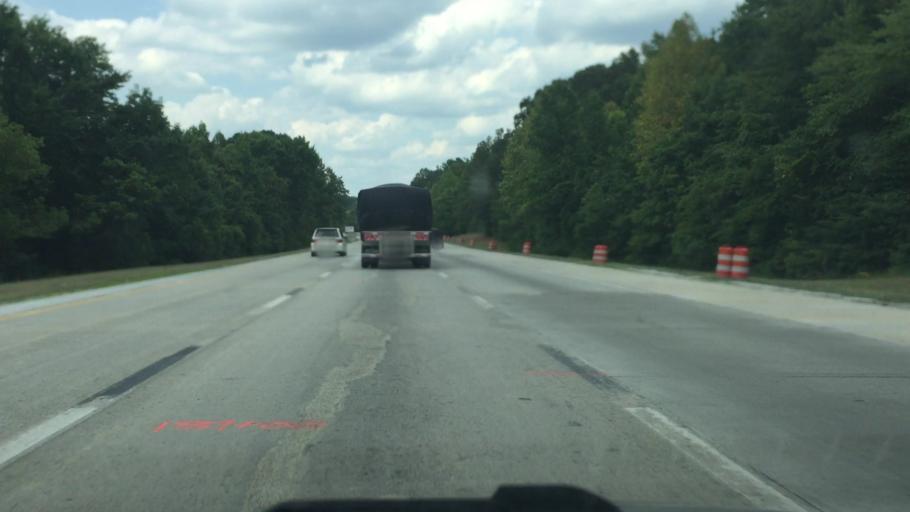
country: US
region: North Carolina
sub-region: Guilford County
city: Jamestown
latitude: 35.9368
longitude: -79.9102
